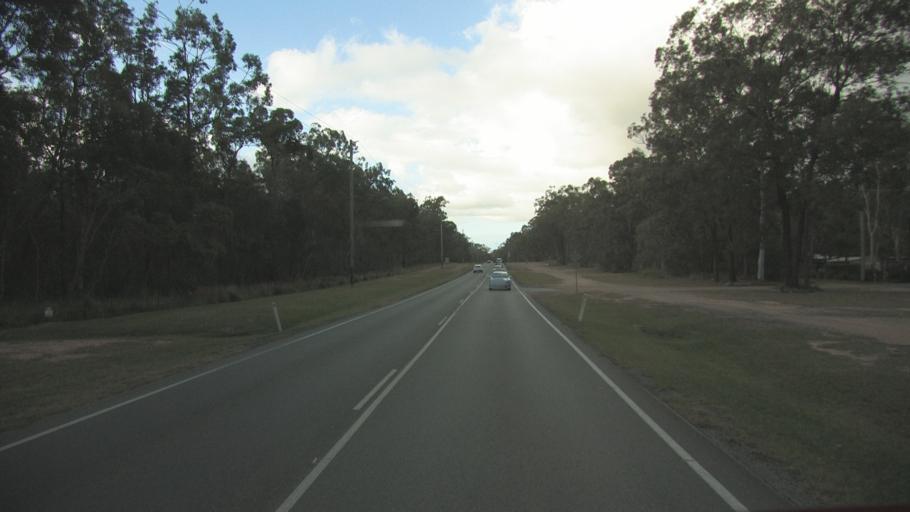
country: AU
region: Queensland
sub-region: Logan
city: Park Ridge South
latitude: -27.7133
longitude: 152.9948
